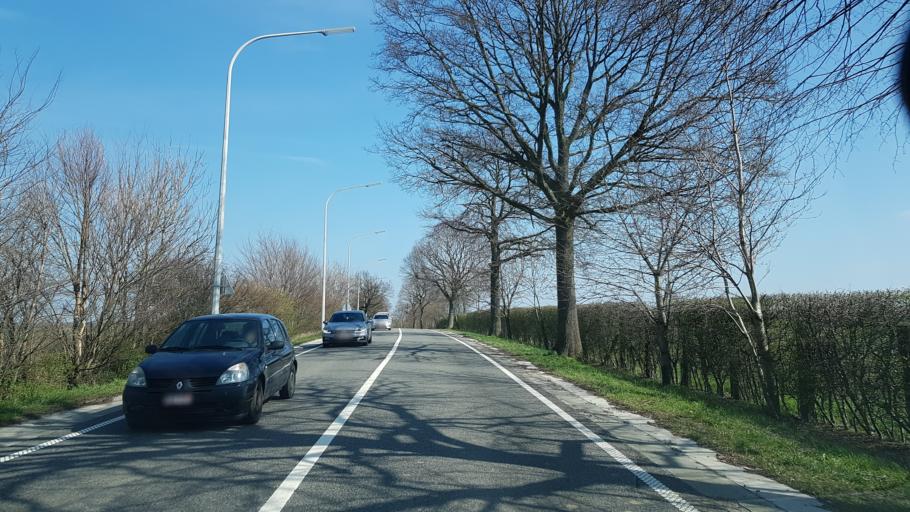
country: BE
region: Wallonia
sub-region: Province de Liege
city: Aubel
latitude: 50.6681
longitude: 5.9004
